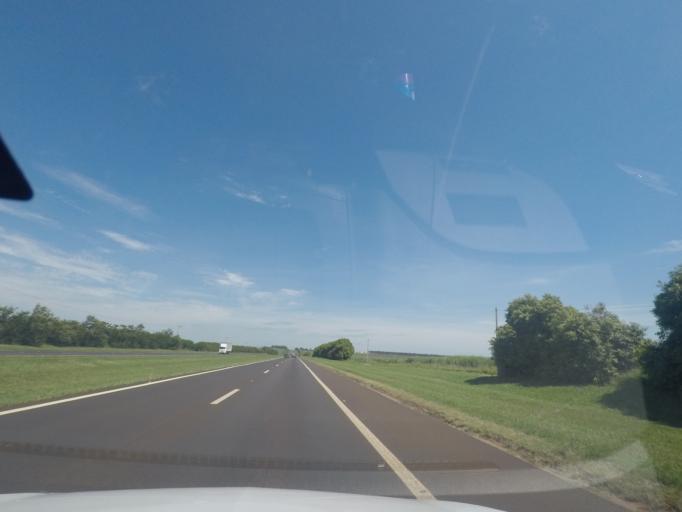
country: BR
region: Sao Paulo
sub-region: Araraquara
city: Araraquara
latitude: -21.8565
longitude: -48.1251
